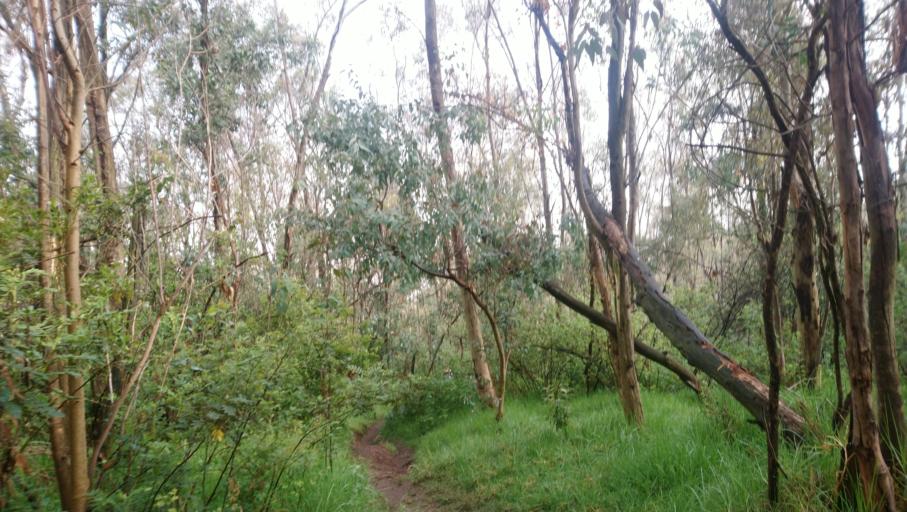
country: MX
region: Mexico
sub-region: Tultitlan
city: Ampliacion San Mateo (Colonia Solidaridad)
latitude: 19.6067
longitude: -99.1224
